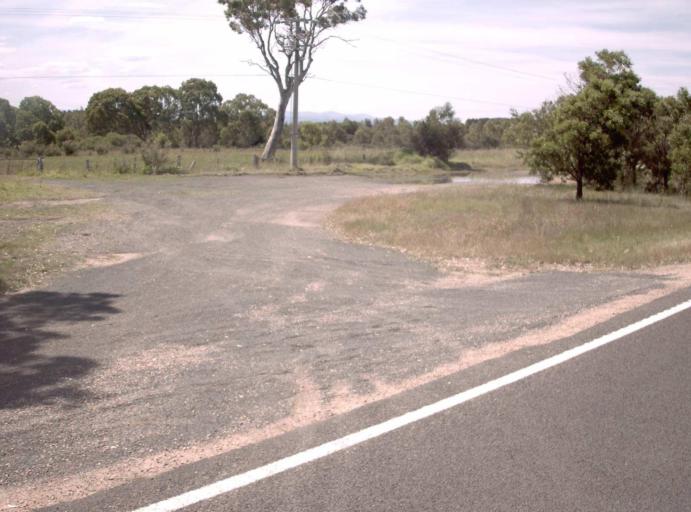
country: AU
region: Victoria
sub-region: Wellington
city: Sale
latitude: -37.9583
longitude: 147.0965
